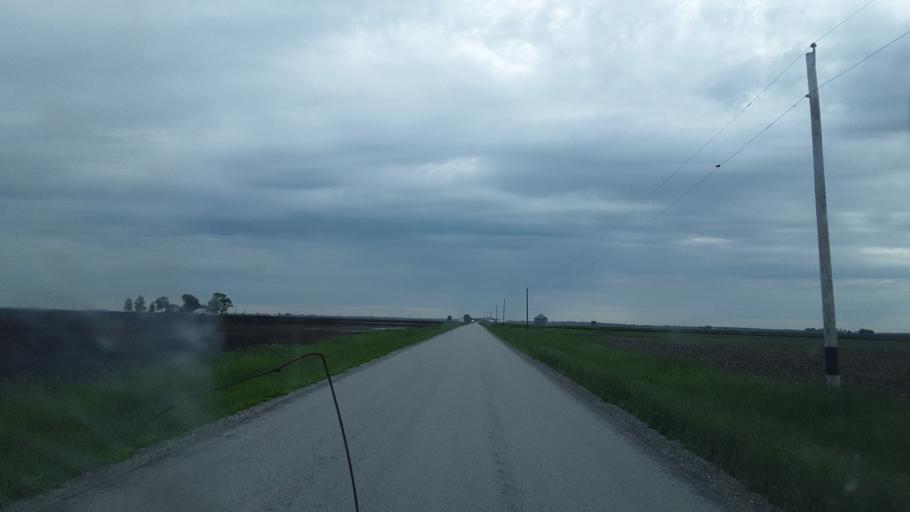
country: US
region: Illinois
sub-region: McDonough County
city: Macomb
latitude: 40.3818
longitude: -90.5534
